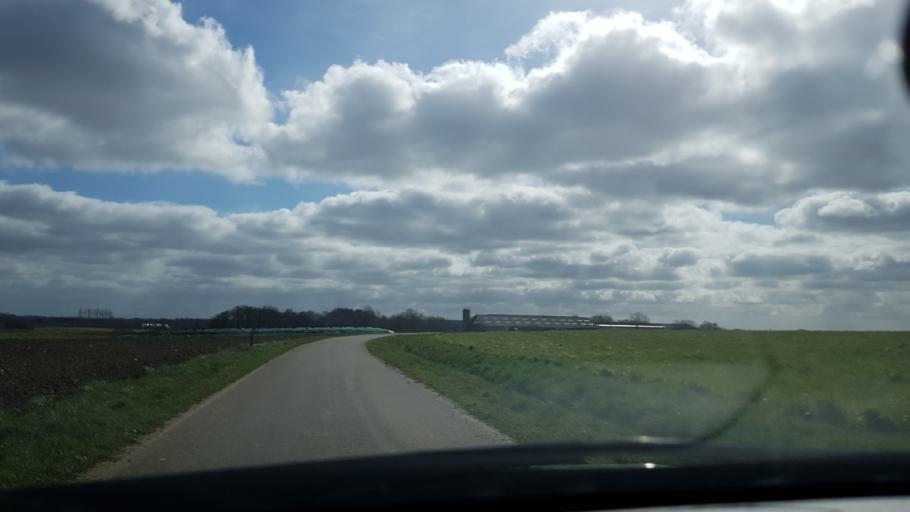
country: DK
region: South Denmark
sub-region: Haderslev Kommune
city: Gram
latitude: 55.3229
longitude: 8.9887
